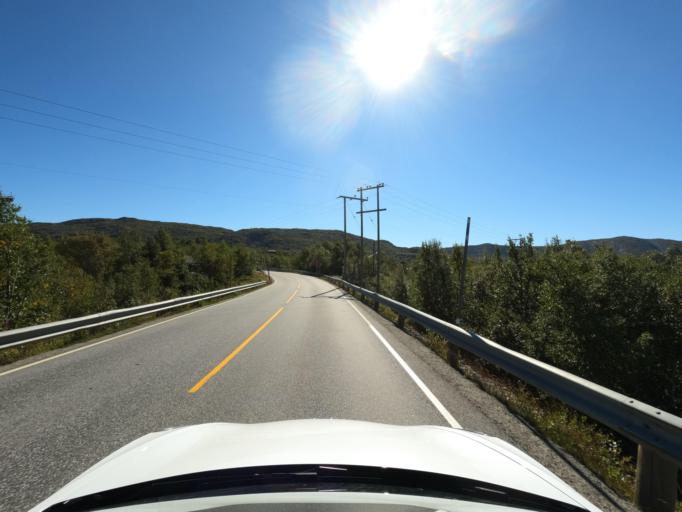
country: NO
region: Buskerud
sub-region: Hol
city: Geilo
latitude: 60.5121
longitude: 7.8510
